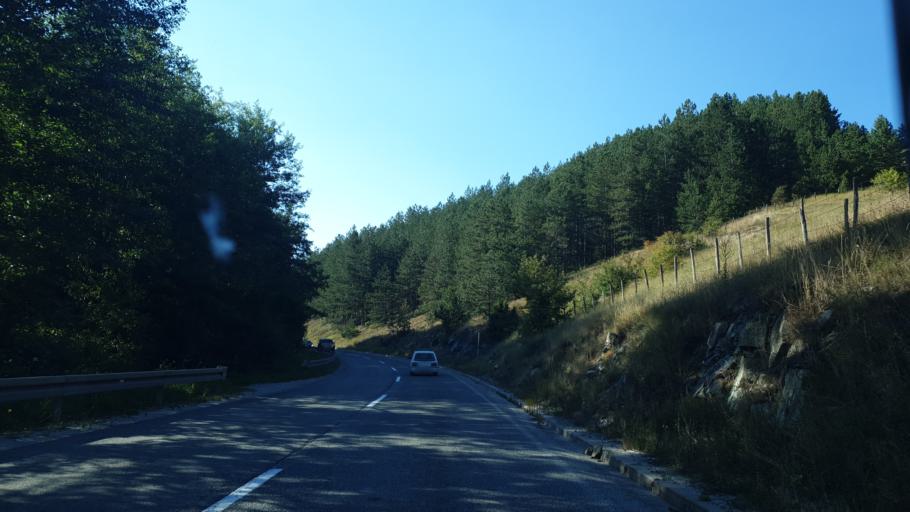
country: RS
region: Central Serbia
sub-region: Zlatiborski Okrug
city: Nova Varos
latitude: 43.5510
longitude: 19.7783
